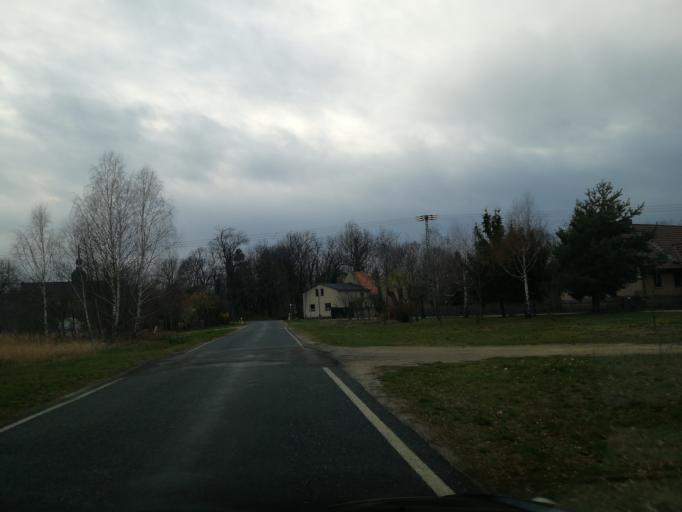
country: DE
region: Brandenburg
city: Vetschau
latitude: 51.7130
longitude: 14.0915
